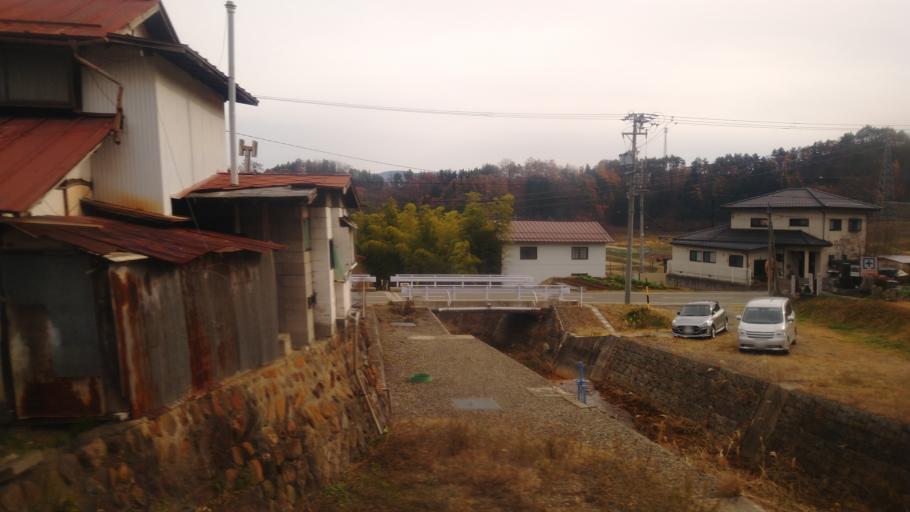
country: JP
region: Nagano
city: Nagano-shi
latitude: 36.5161
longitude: 138.0742
